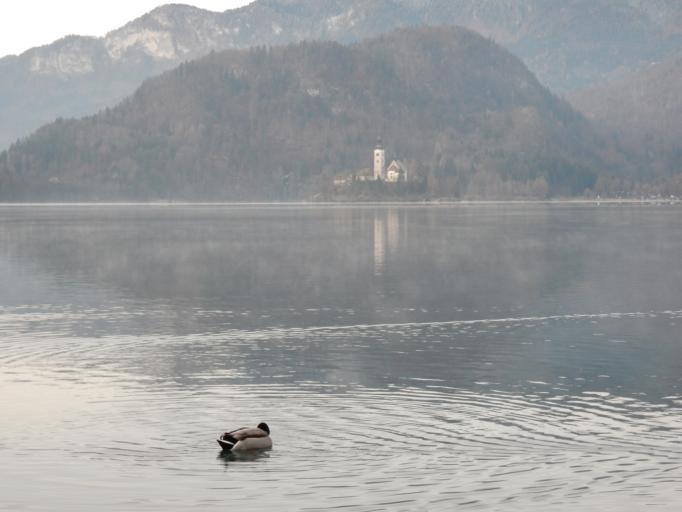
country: SI
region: Bled
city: Bled
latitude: 46.3694
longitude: 14.1068
